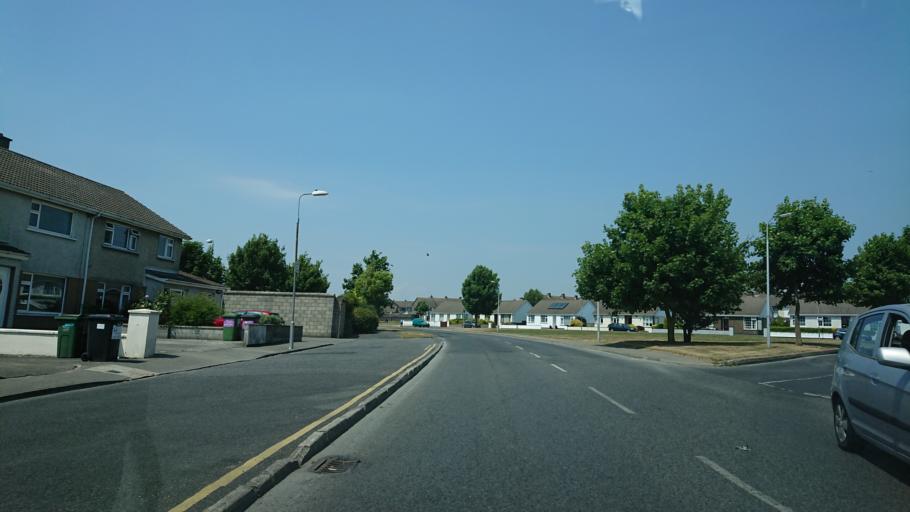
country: IE
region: Munster
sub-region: Waterford
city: Waterford
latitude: 52.2466
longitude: -7.1352
